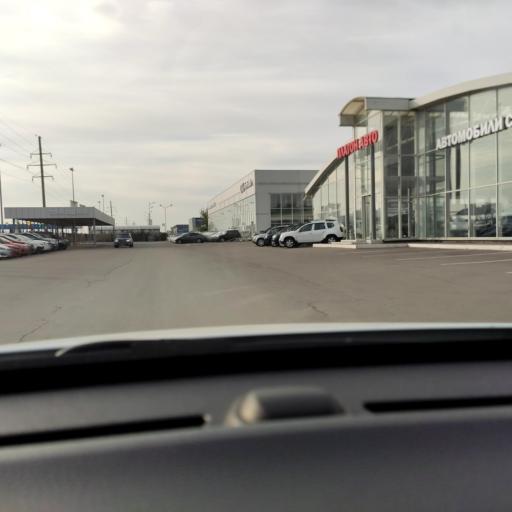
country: RU
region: Voronezj
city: Somovo
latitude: 51.6657
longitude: 39.3000
